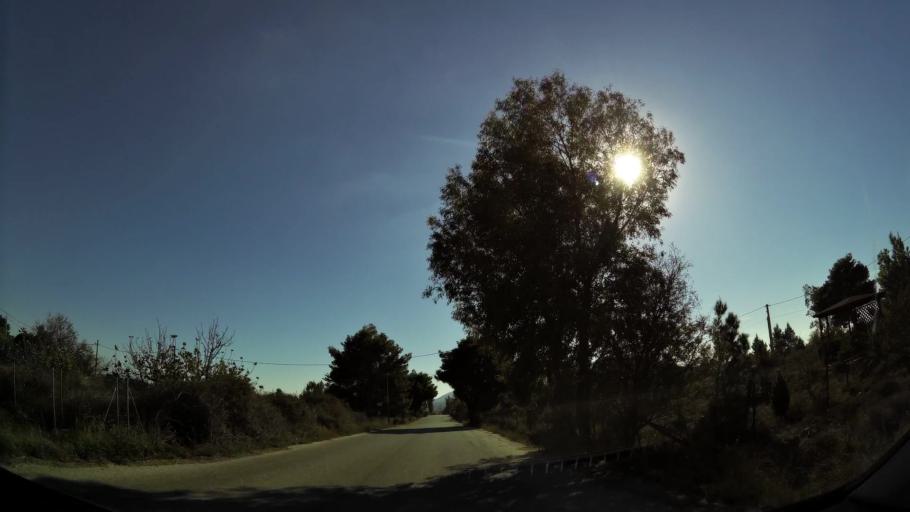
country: GR
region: Attica
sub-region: Nomarchia Anatolikis Attikis
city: Anthousa
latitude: 38.0259
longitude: 23.8683
